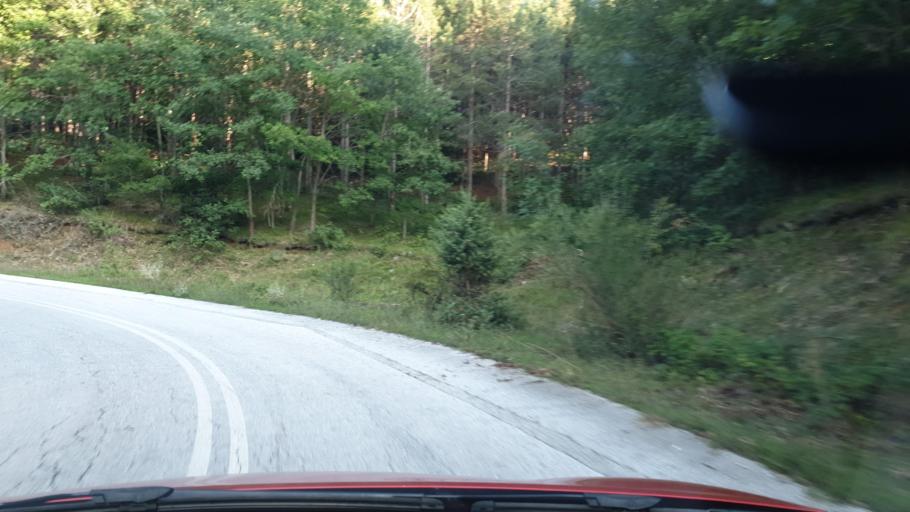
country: GR
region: Central Macedonia
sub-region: Nomos Chalkidikis
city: Galatista
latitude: 40.5058
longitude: 23.2477
